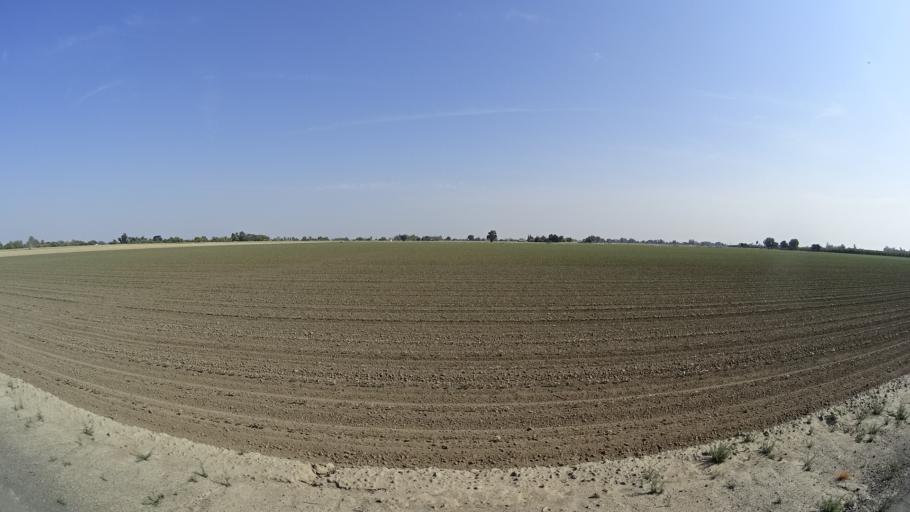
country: US
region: California
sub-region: Kings County
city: Lemoore Station
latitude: 36.3270
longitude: -119.8668
